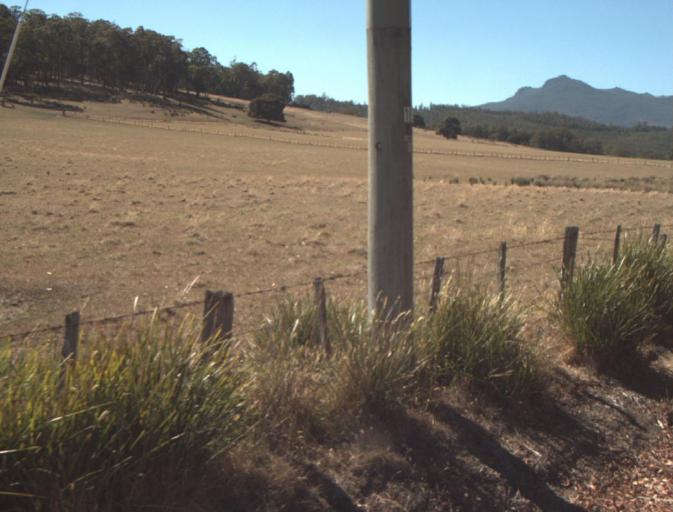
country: AU
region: Tasmania
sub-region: Launceston
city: Newstead
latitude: -41.3069
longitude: 147.3183
